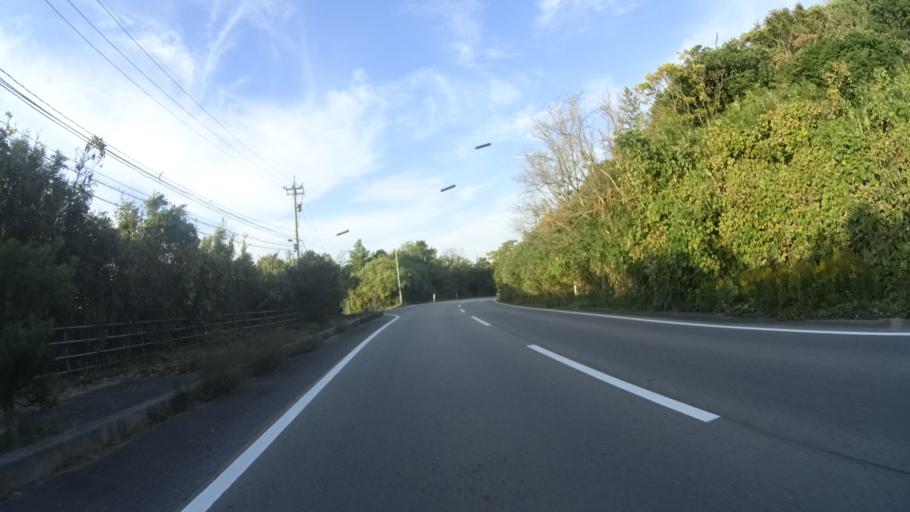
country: JP
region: Ishikawa
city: Hakui
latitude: 37.1128
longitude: 136.7278
